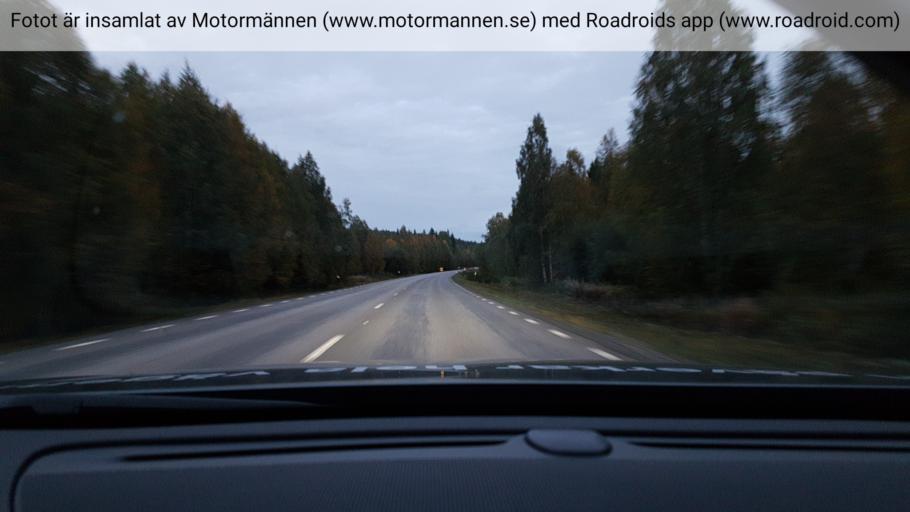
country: SE
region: Norrbotten
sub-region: Alvsbyns Kommun
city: AElvsbyn
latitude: 65.7820
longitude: 20.8070
